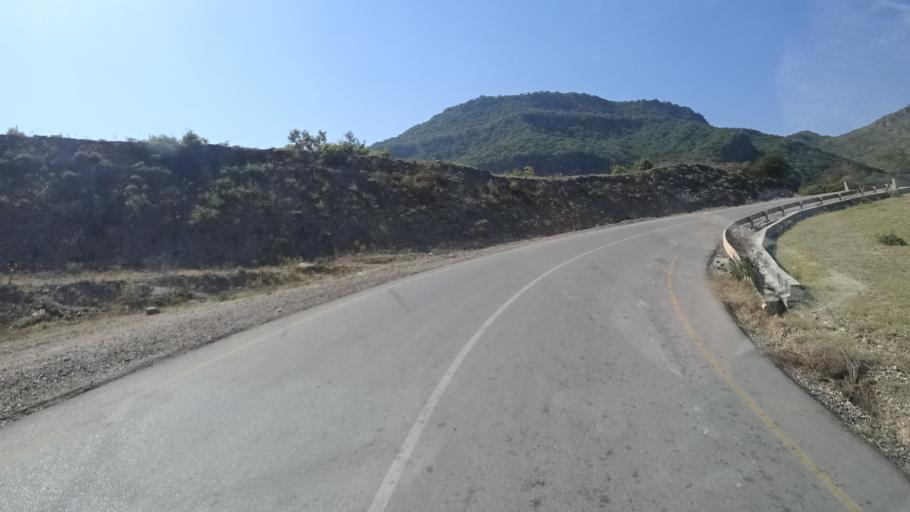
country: OM
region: Zufar
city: Salalah
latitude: 17.0504
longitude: 54.6110
